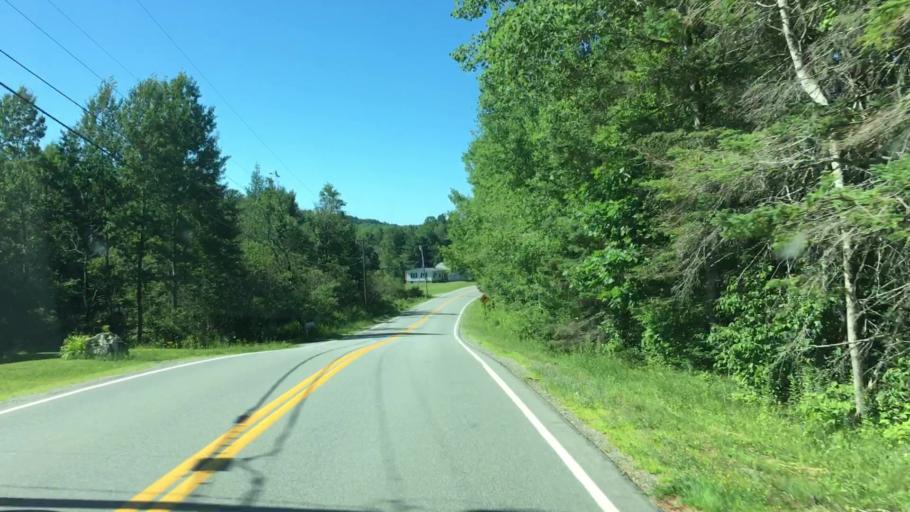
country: US
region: Maine
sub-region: Hancock County
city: Dedham
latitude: 44.7228
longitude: -68.6395
